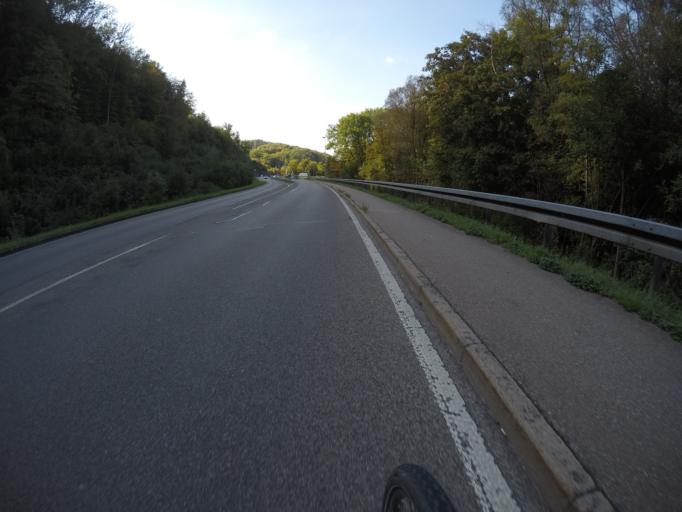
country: DE
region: Baden-Wuerttemberg
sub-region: Regierungsbezirk Stuttgart
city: Esslingen
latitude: 48.7251
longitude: 9.3236
